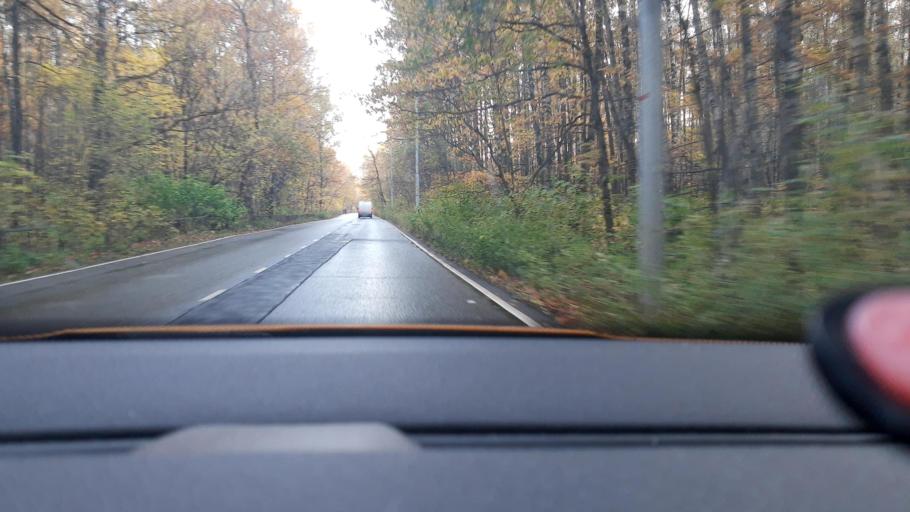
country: RU
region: Moskovskaya
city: Bogorodskoye
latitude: 55.8310
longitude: 37.7458
